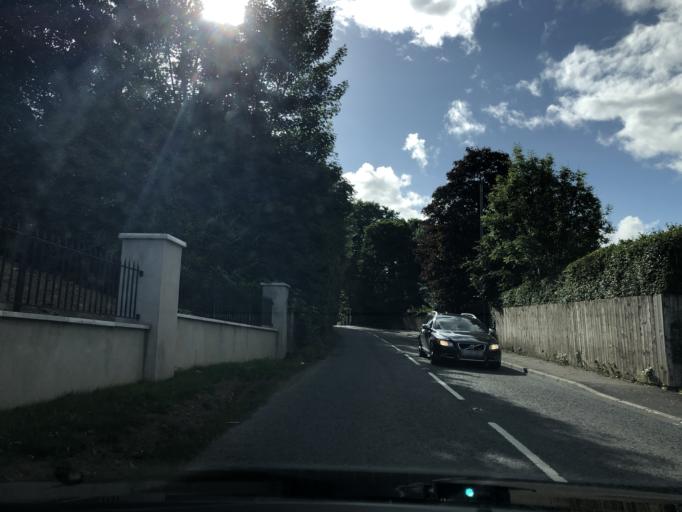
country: GB
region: Northern Ireland
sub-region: Castlereagh District
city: Dundonald
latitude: 54.5863
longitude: -5.8016
